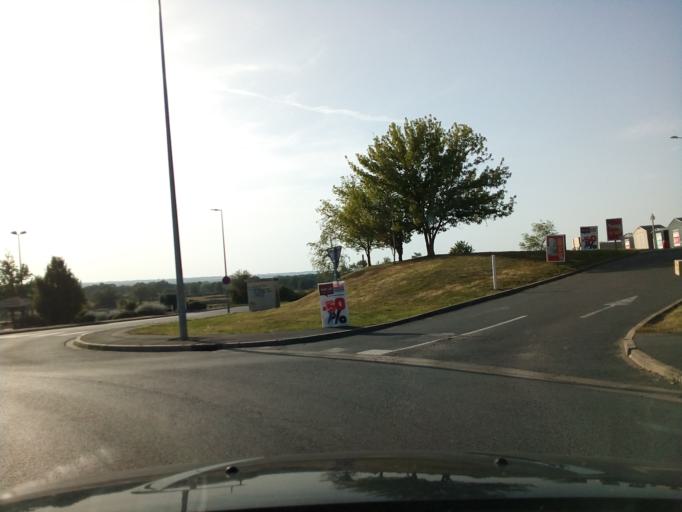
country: FR
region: Auvergne
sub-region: Departement de l'Allier
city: Domerat
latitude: 46.3680
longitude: 2.5666
